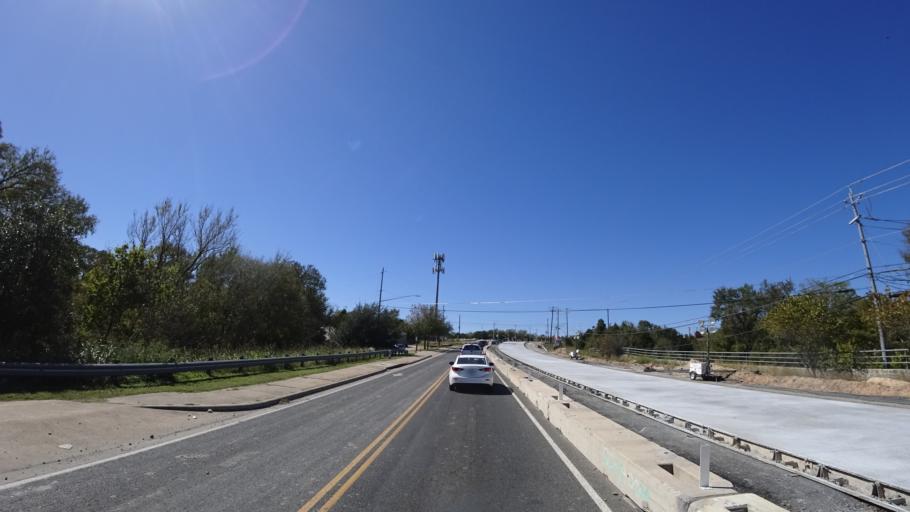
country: US
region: Texas
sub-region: Travis County
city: Austin
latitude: 30.3027
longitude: -97.6585
